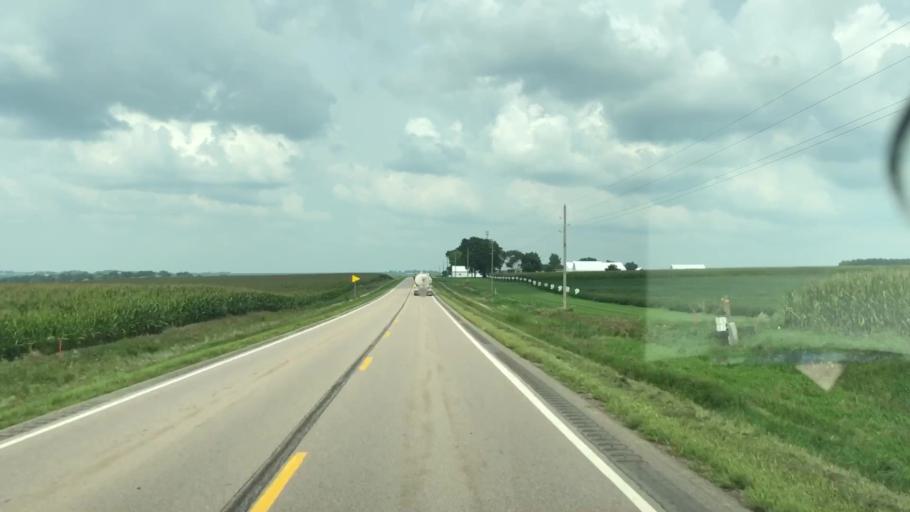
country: US
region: Iowa
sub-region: Plymouth County
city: Remsen
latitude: 42.8005
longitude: -95.9577
